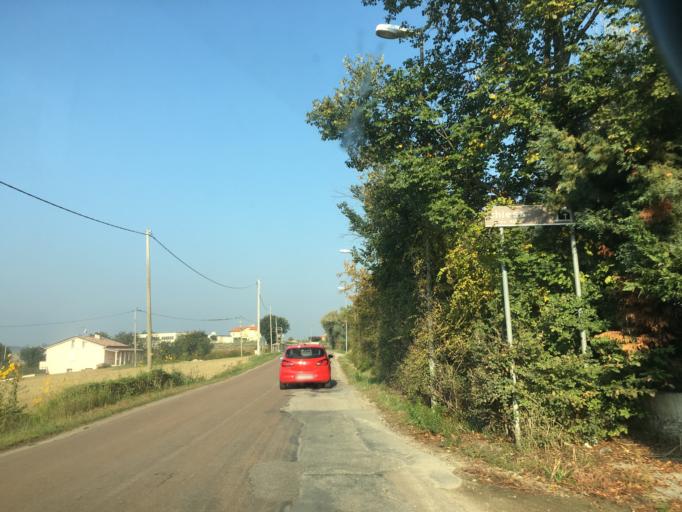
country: IT
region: Emilia-Romagna
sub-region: Provincia di Rimini
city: San Clemente
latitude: 43.9466
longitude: 12.6175
